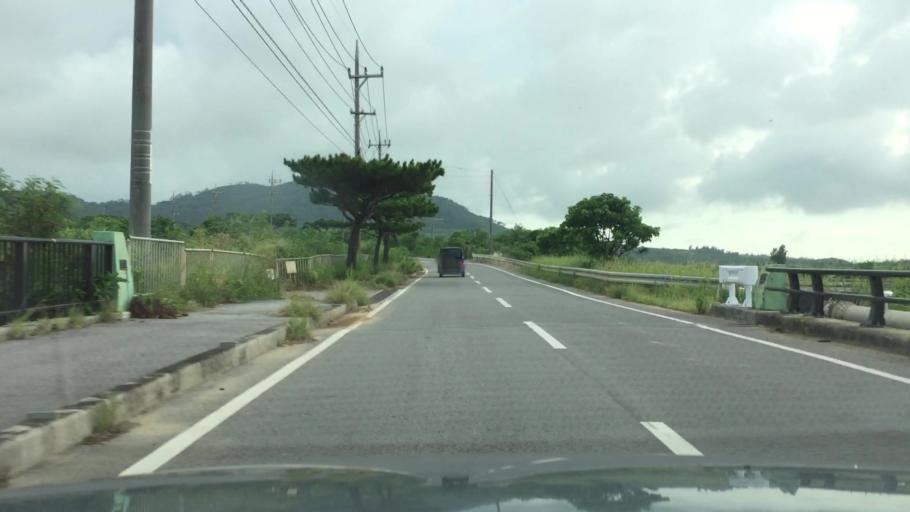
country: JP
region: Okinawa
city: Ishigaki
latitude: 24.3886
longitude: 124.1532
